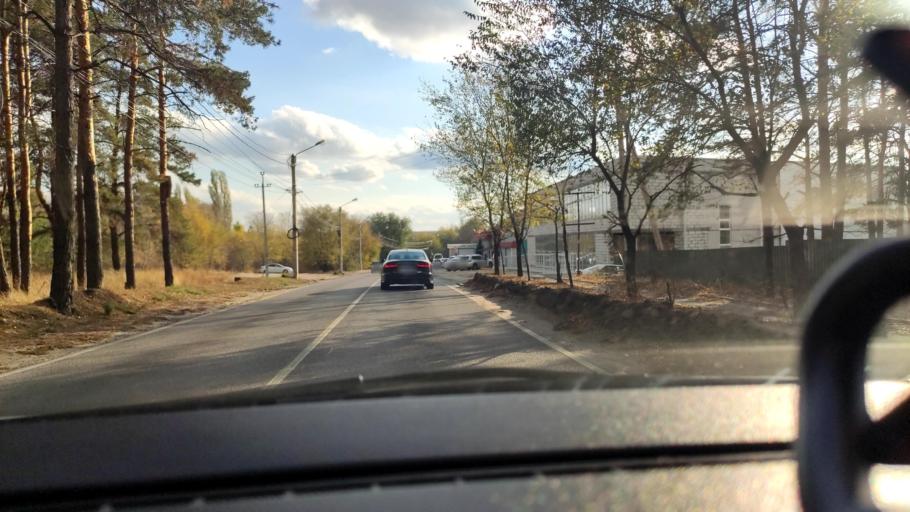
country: RU
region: Voronezj
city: Pridonskoy
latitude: 51.6469
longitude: 39.0982
